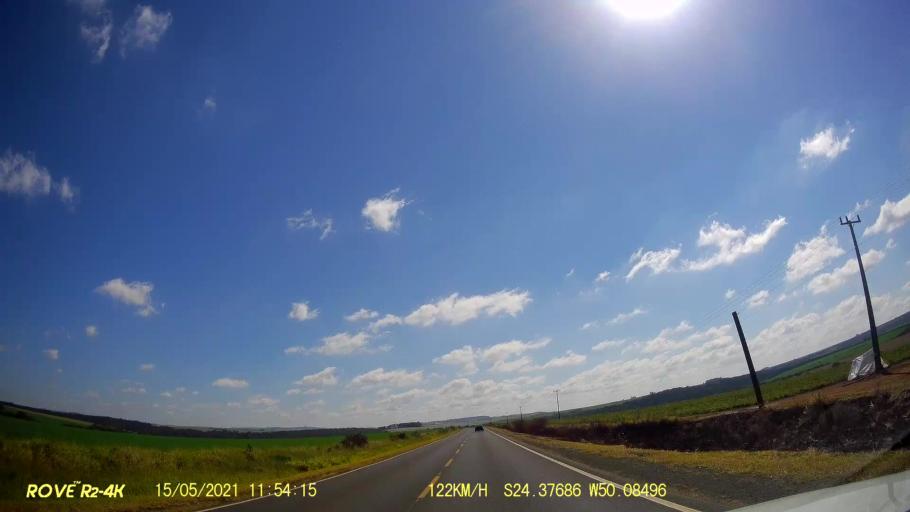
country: BR
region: Parana
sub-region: Pirai Do Sul
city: Pirai do Sul
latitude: -24.3769
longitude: -50.0849
